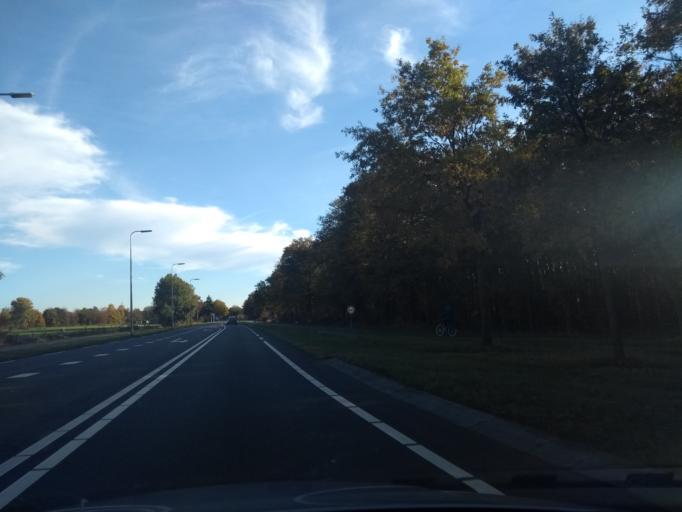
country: NL
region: Overijssel
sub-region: Gemeente Borne
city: Borne
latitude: 52.3305
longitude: 6.7098
